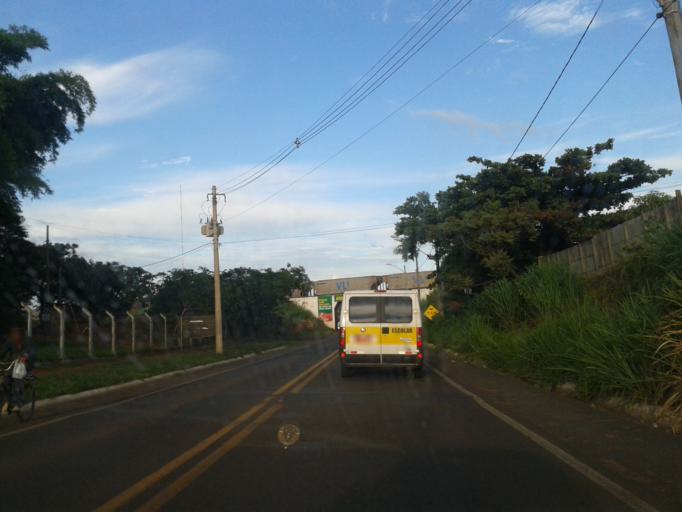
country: BR
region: Minas Gerais
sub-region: Araguari
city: Araguari
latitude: -18.6419
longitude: -48.2159
